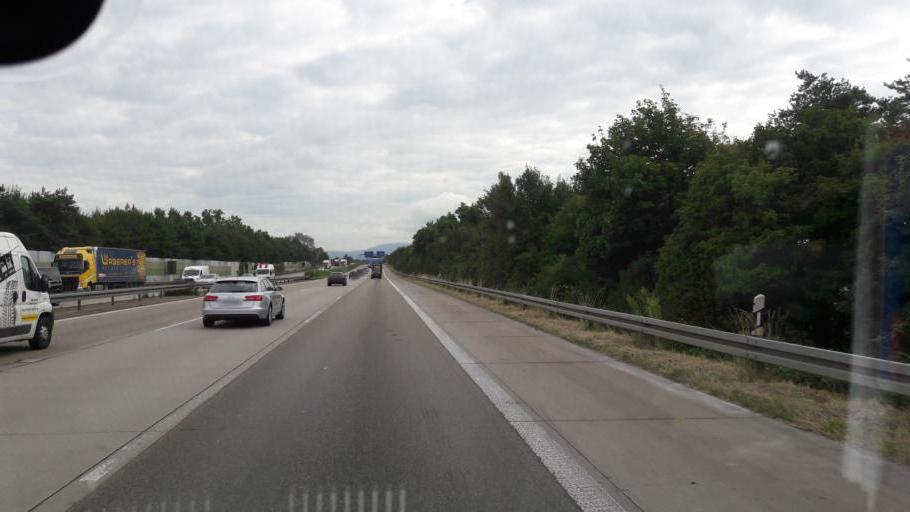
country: DE
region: Baden-Wuerttemberg
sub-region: Karlsruhe Region
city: Sankt Leon-Rot
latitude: 49.2624
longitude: 8.6069
